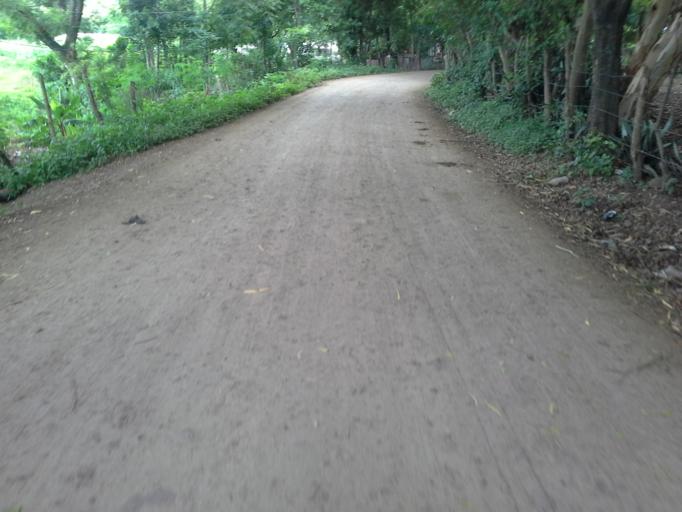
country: NI
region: Matagalpa
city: Ciudad Dario
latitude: 12.6991
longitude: -86.0485
